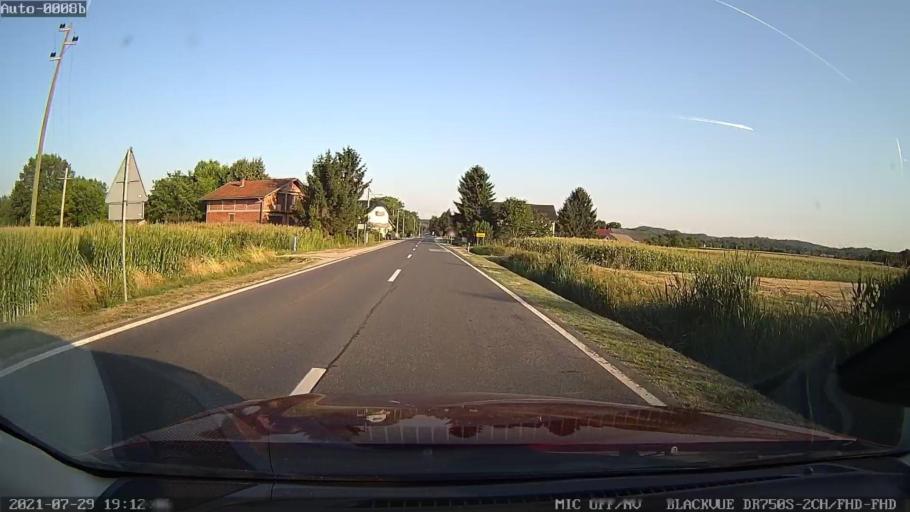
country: HR
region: Varazdinska
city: Jalzabet
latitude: 46.2704
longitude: 16.5142
